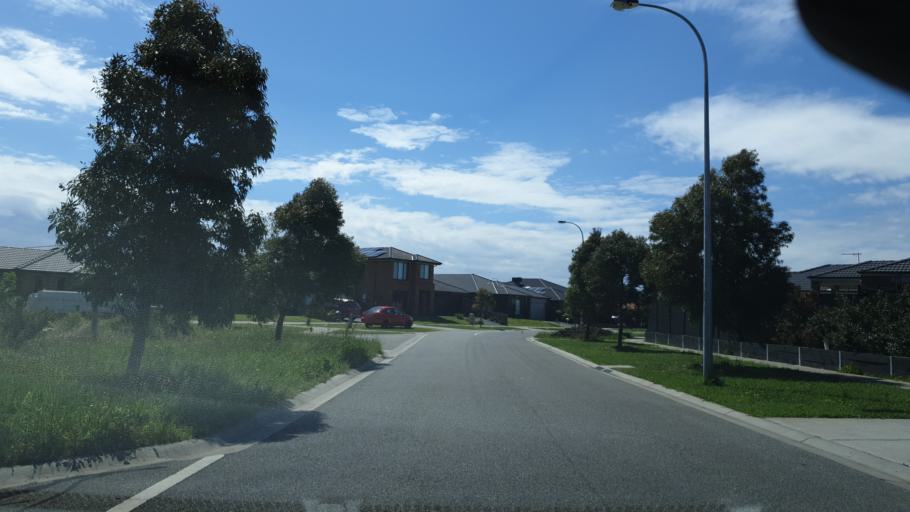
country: AU
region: Victoria
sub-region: Casey
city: Cranbourne East
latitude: -38.0976
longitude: 145.3078
